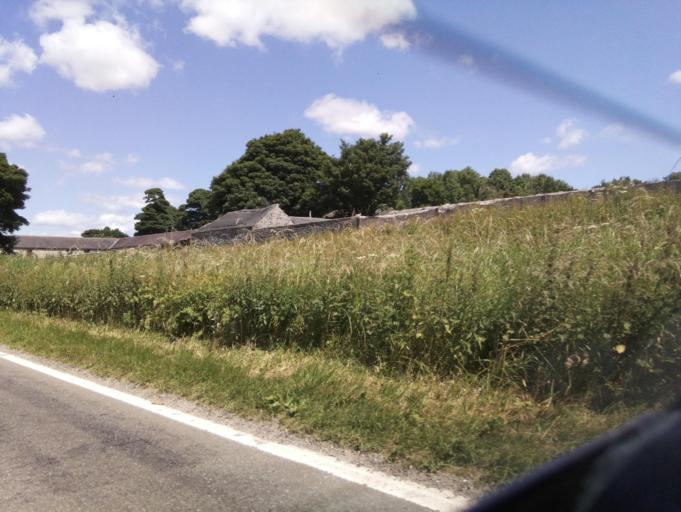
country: GB
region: England
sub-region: Derbyshire
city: Ashbourne
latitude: 53.1252
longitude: -1.7534
